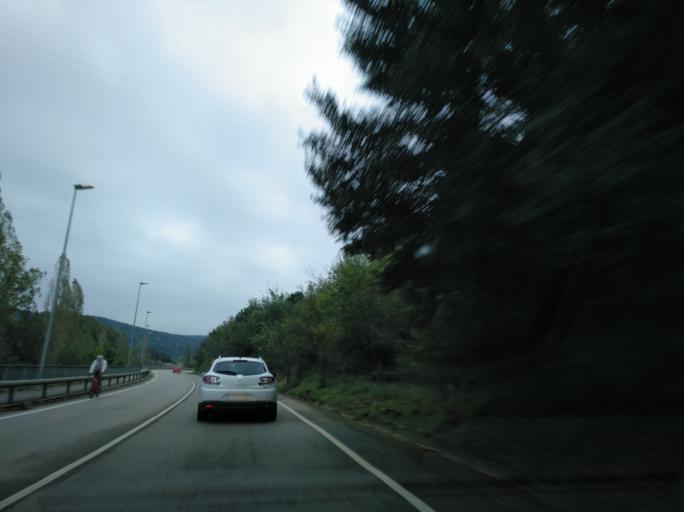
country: ES
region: Catalonia
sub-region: Provincia de Girona
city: Girona
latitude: 41.9724
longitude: 2.8330
